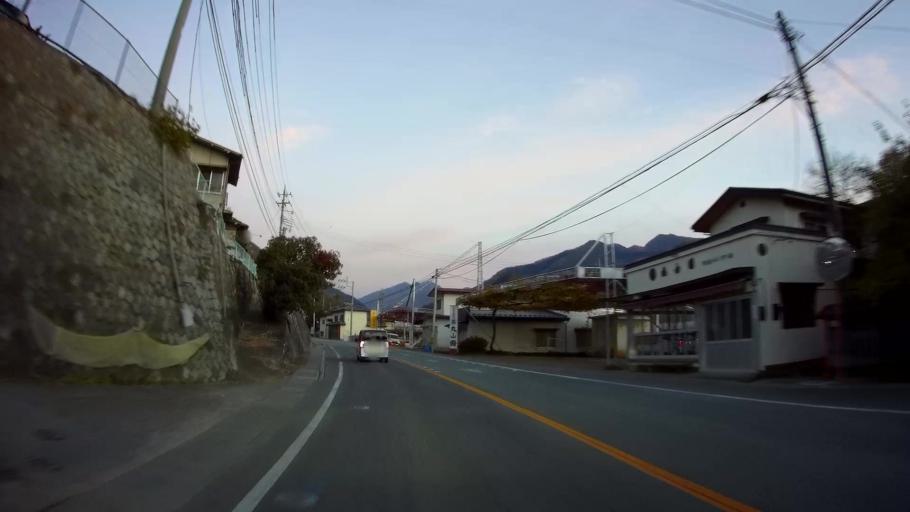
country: JP
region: Yamanashi
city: Enzan
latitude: 35.6587
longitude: 138.7356
